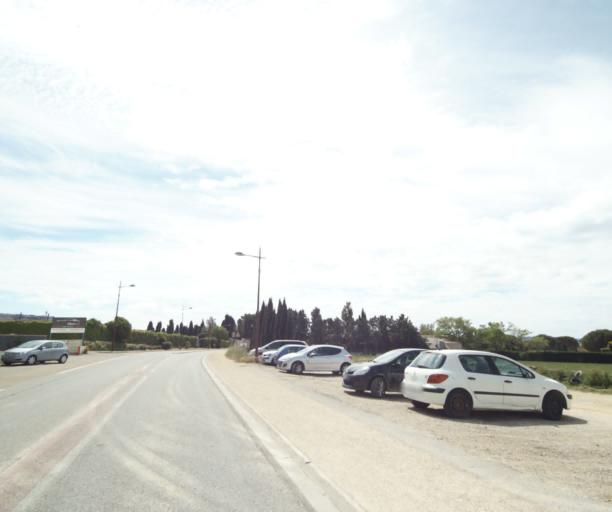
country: FR
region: Provence-Alpes-Cote d'Azur
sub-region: Departement des Bouches-du-Rhone
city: Rognac
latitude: 43.4955
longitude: 5.2299
